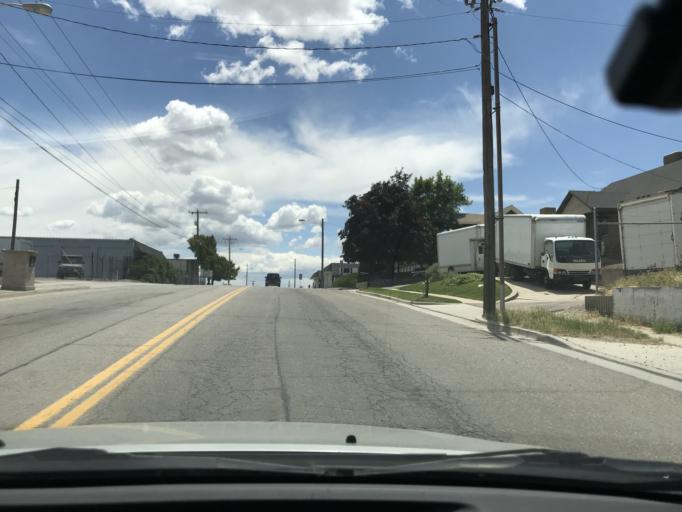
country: US
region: Utah
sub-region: Salt Lake County
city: Centerfield
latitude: 40.6778
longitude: -111.8998
